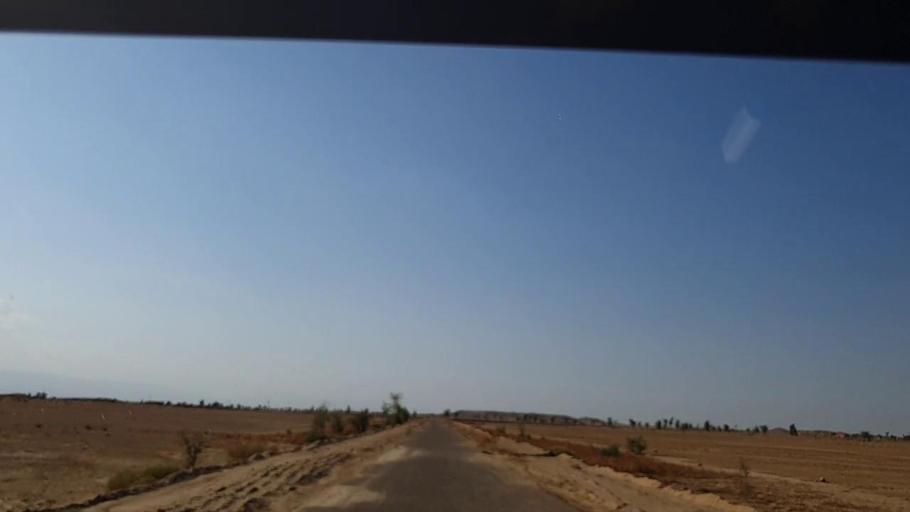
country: PK
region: Sindh
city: Johi
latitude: 26.5285
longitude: 67.5092
